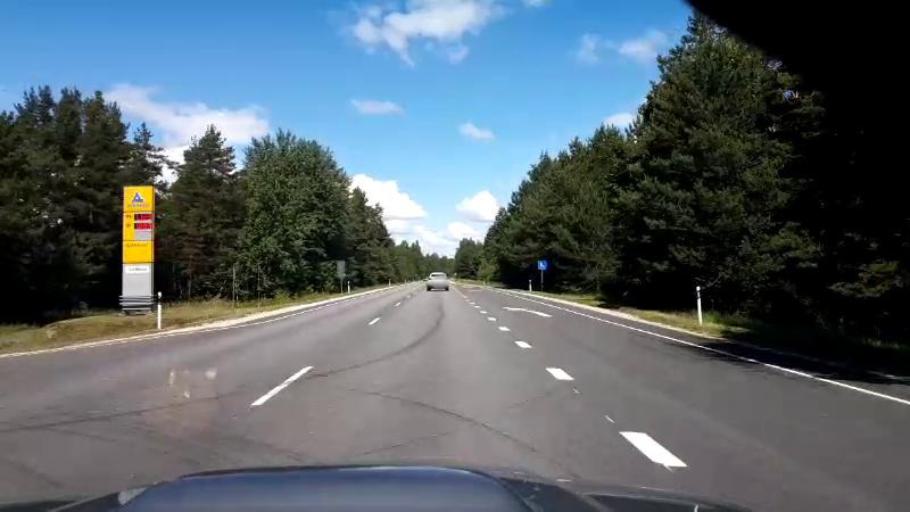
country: EE
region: Paernumaa
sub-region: Paernu linn
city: Parnu
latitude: 58.2136
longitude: 24.4862
